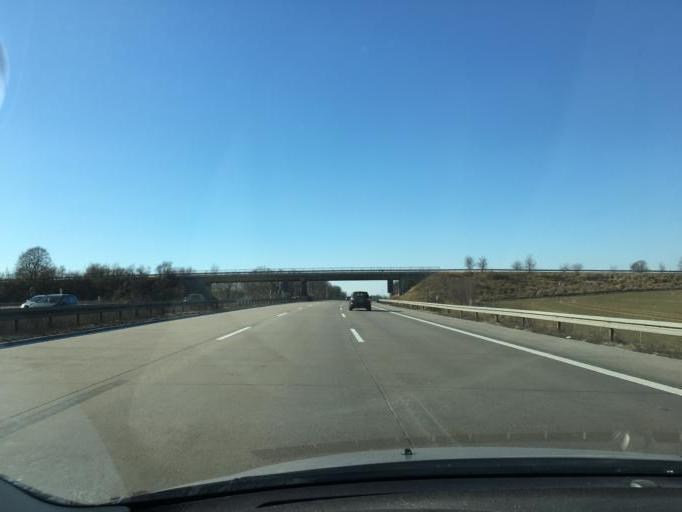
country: DE
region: Saxony
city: Reinsberg
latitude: 51.0588
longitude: 13.3977
